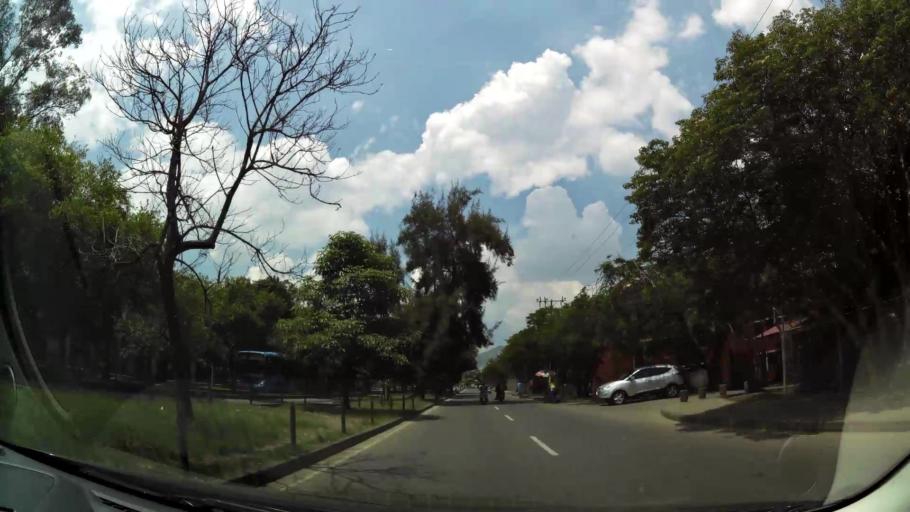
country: CO
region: Valle del Cauca
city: Cali
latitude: 3.4174
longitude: -76.5482
